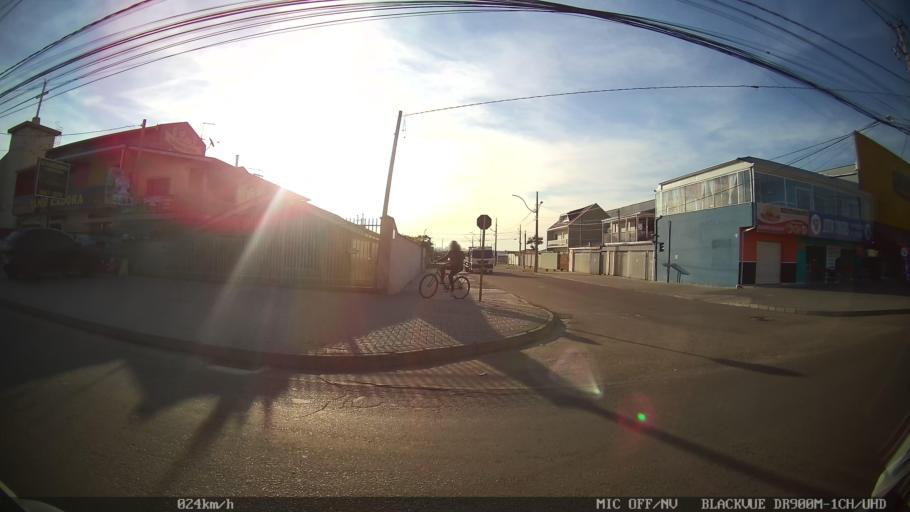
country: BR
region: Parana
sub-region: Pinhais
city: Pinhais
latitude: -25.4584
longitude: -49.1582
